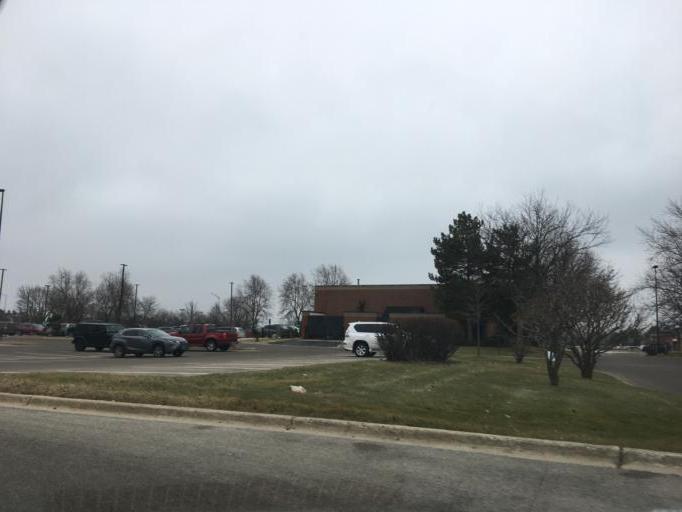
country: US
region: Illinois
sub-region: McHenry County
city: Crystal Lake
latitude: 42.2273
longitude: -88.3098
